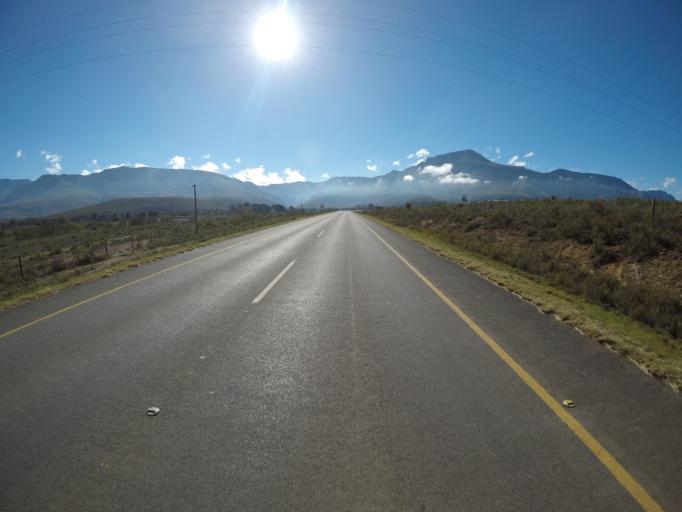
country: ZA
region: Western Cape
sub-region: Overberg District Municipality
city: Caledon
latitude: -34.0569
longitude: 19.5588
